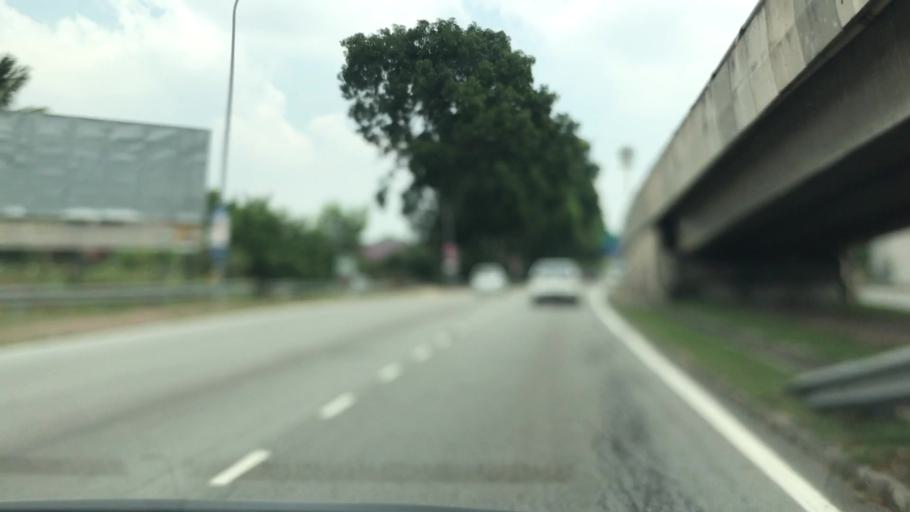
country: MY
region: Selangor
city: Subang Jaya
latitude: 3.0493
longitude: 101.6410
